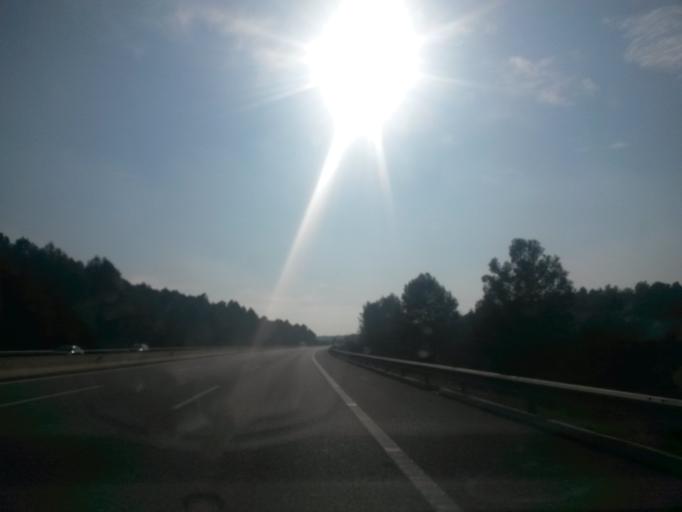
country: ES
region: Catalonia
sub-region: Provincia de Girona
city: Bascara
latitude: 42.1464
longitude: 2.9187
